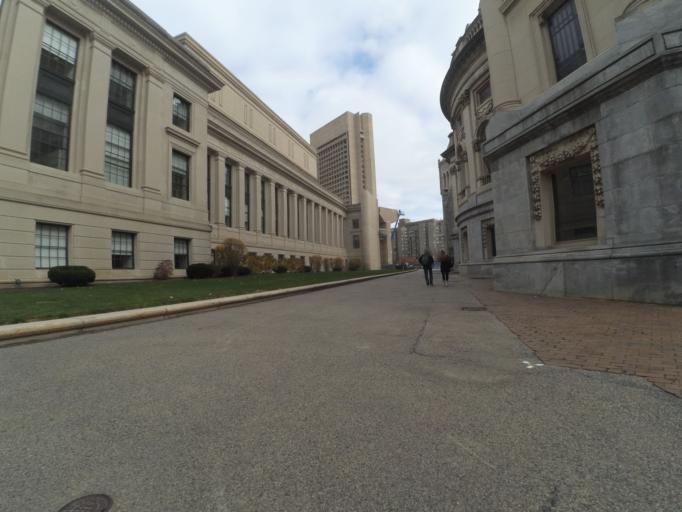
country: US
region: Massachusetts
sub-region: Suffolk County
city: Boston
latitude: 42.3448
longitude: -71.0853
